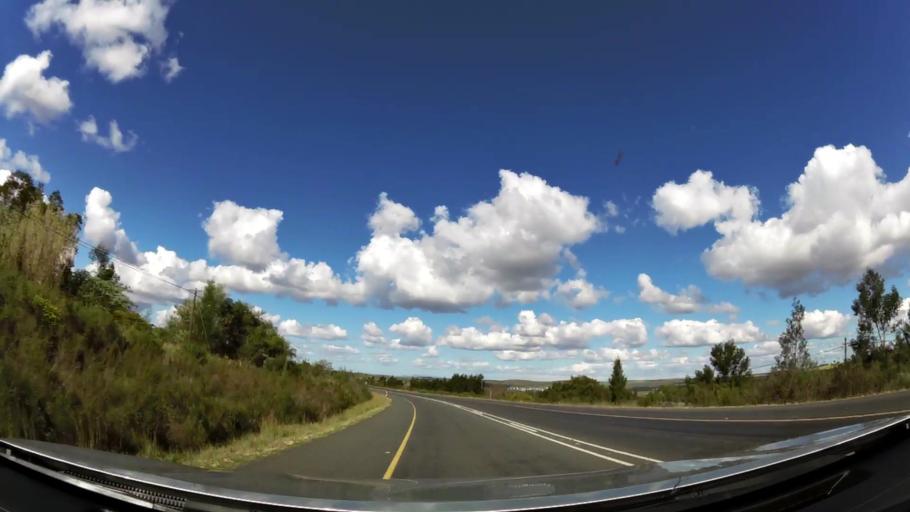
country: ZA
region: Western Cape
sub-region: Overberg District Municipality
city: Swellendam
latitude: -34.0326
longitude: 20.4206
